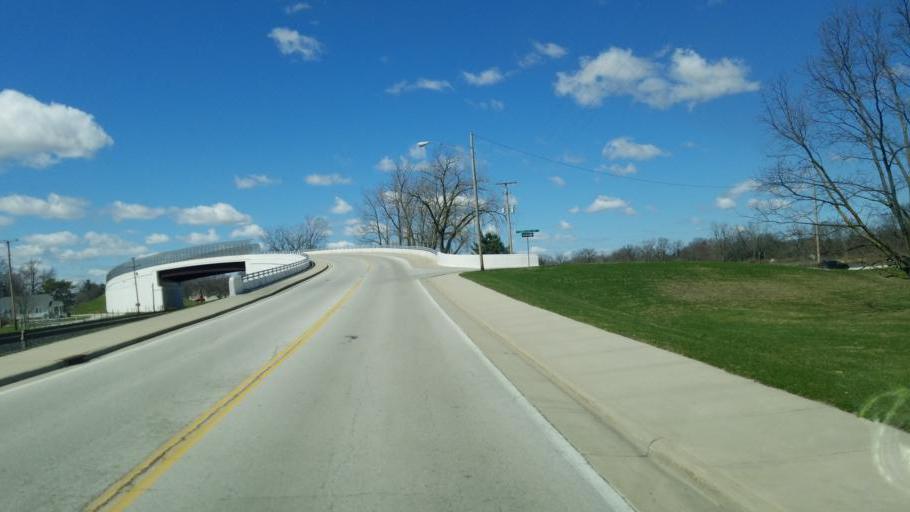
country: US
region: Ohio
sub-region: Seneca County
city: Fostoria
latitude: 41.1562
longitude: -83.4303
